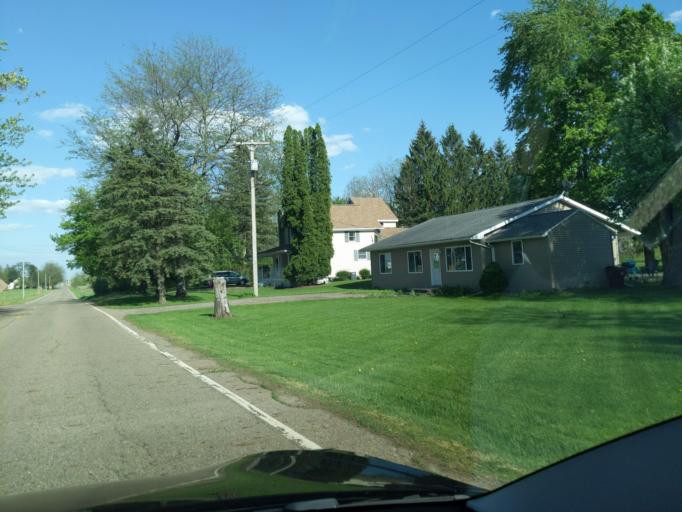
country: US
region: Michigan
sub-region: Eaton County
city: Dimondale
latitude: 42.6829
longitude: -84.6926
